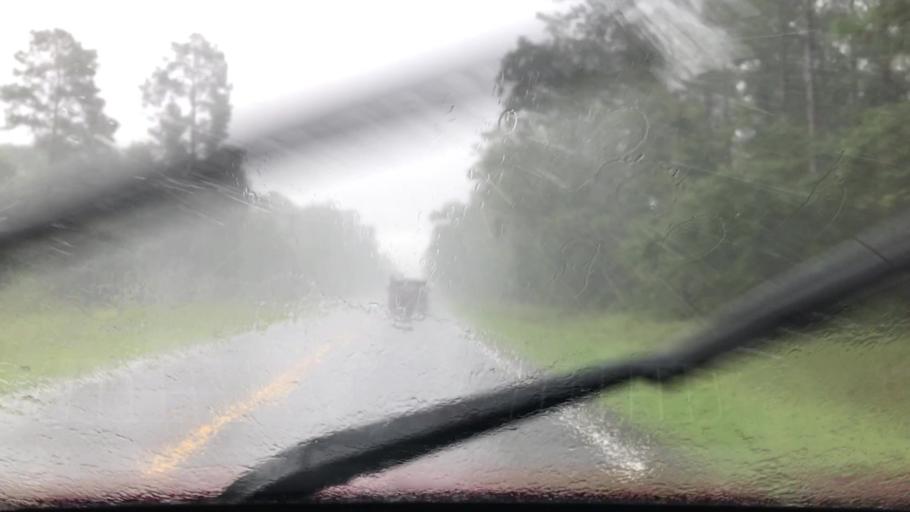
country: US
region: South Carolina
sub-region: Horry County
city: Red Hill
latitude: 33.9036
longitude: -78.9069
